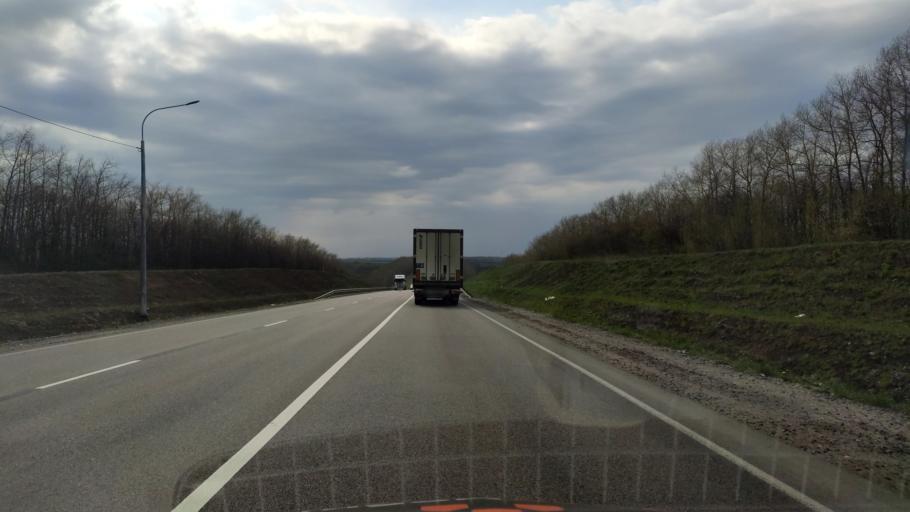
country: RU
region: Voronezj
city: Nizhnedevitsk
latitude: 51.5596
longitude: 38.2447
